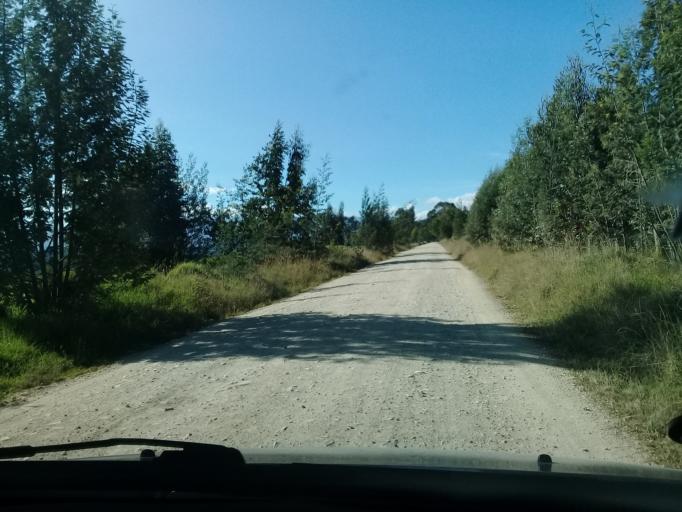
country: CO
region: Cundinamarca
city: Guasca
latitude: 4.9152
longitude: -73.8854
